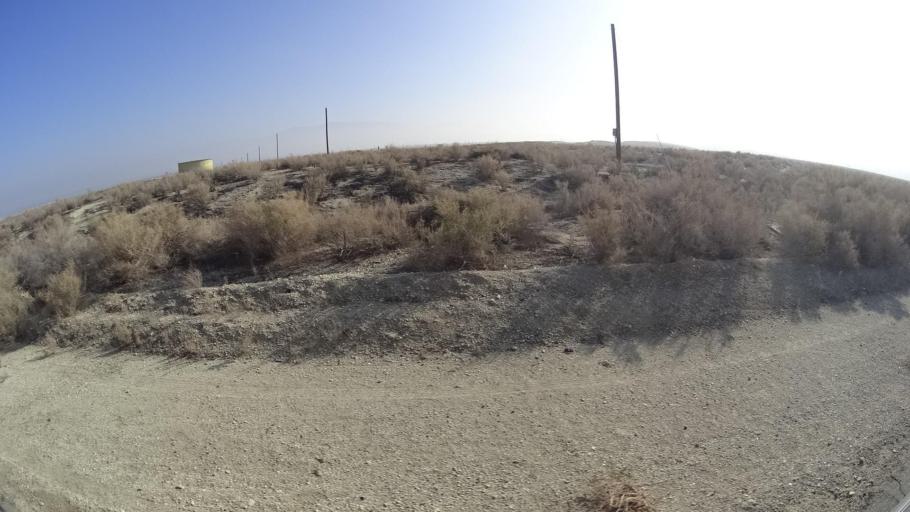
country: US
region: California
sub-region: Kern County
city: Maricopa
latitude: 35.1003
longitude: -119.3970
